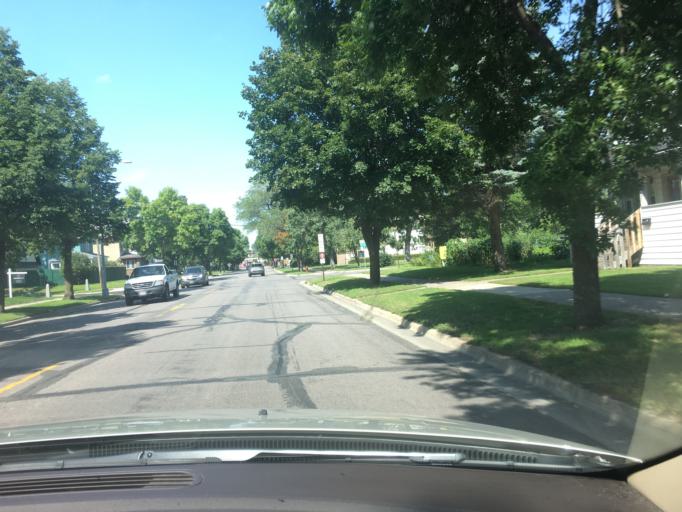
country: US
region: Minnesota
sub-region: Stearns County
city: Saint Cloud
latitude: 45.5544
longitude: -94.1546
